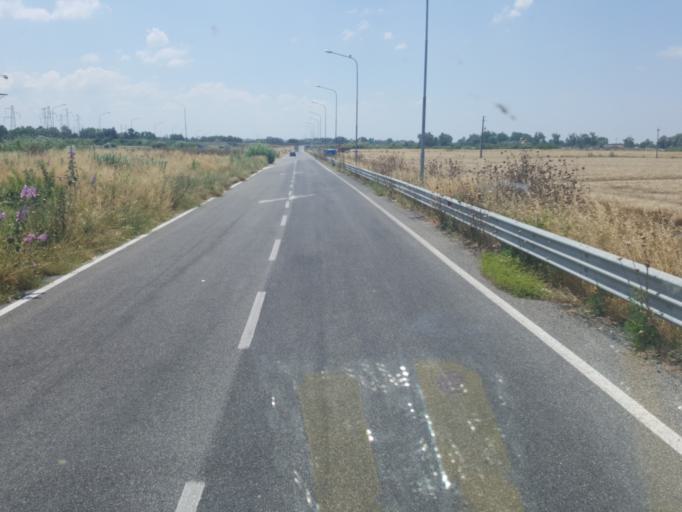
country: IT
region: Latium
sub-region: Citta metropolitana di Roma Capitale
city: Fiano Romano
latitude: 42.1600
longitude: 12.6434
